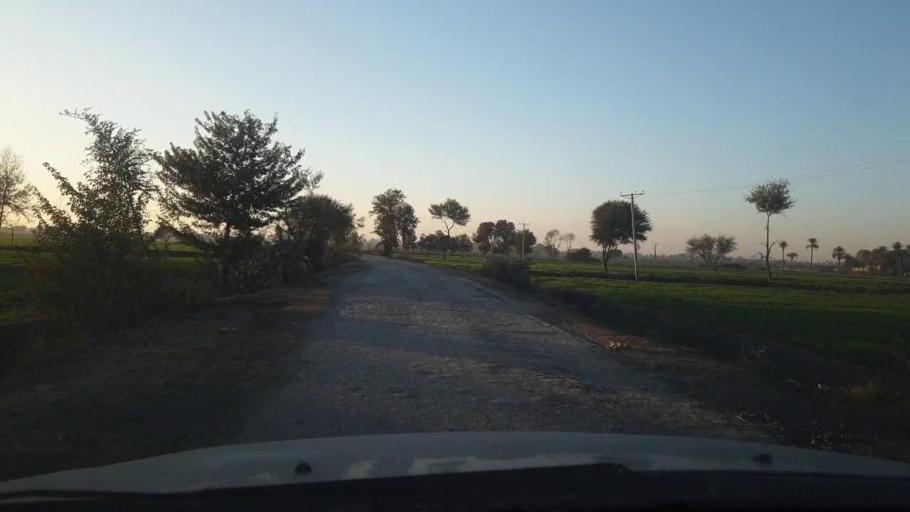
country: PK
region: Sindh
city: Pano Aqil
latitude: 27.9129
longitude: 69.1969
